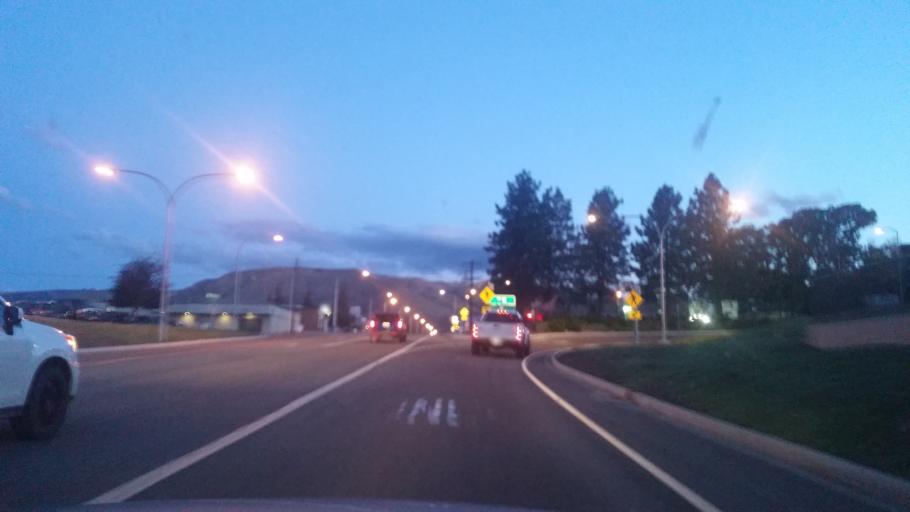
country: US
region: Washington
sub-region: Douglas County
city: East Wenatchee
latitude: 47.4094
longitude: -120.3001
